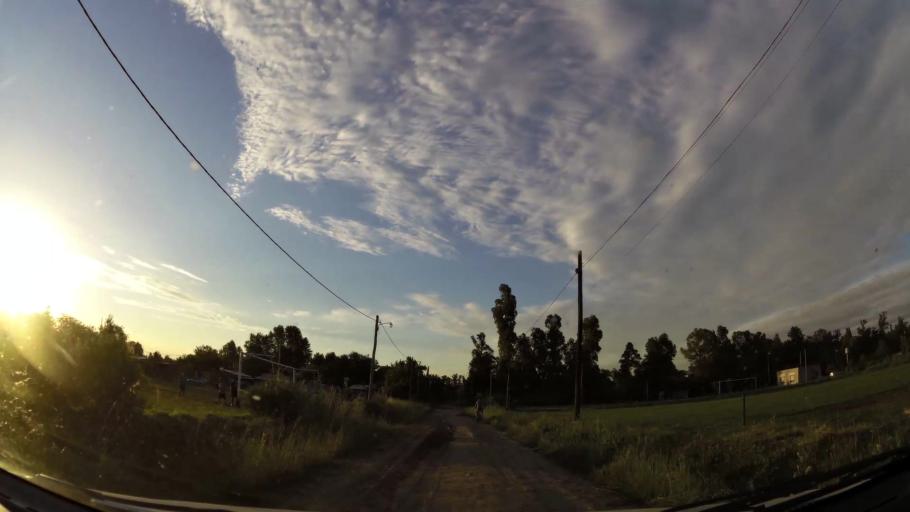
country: AR
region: Buenos Aires
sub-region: Partido de Merlo
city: Merlo
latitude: -34.6703
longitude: -58.7764
